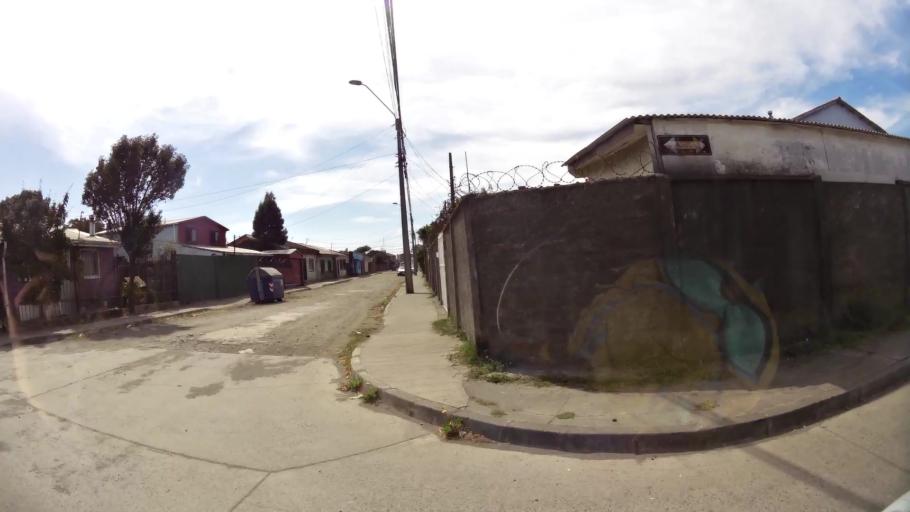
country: CL
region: Biobio
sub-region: Provincia de Concepcion
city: Talcahuano
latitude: -36.7221
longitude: -73.1160
